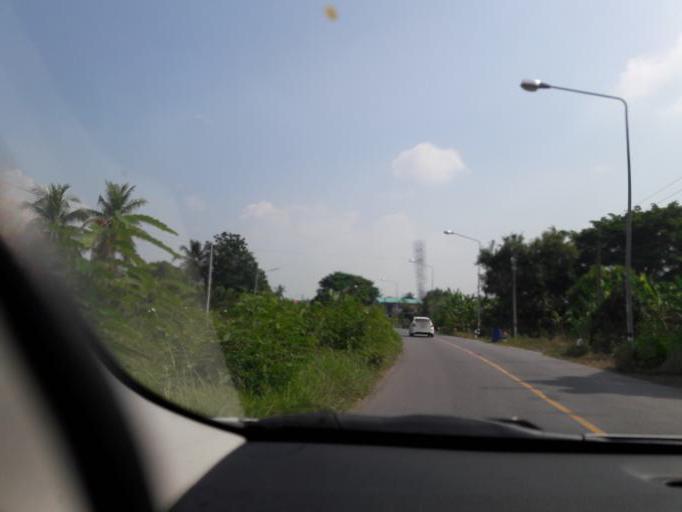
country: TH
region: Ang Thong
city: Ang Thong
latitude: 14.6007
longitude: 100.3990
